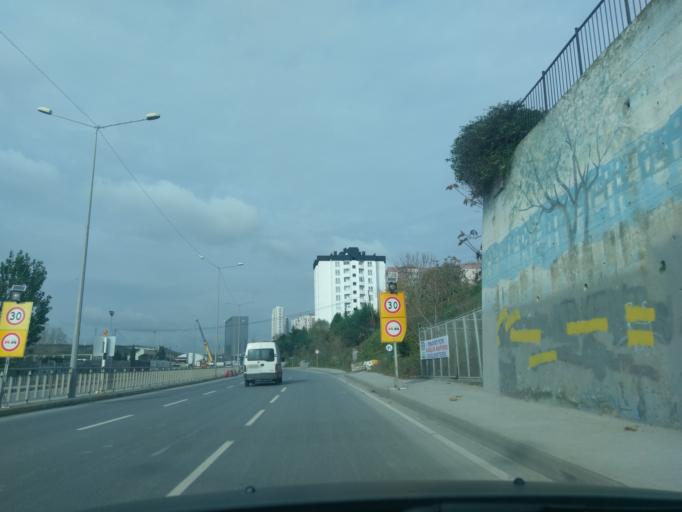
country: TR
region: Istanbul
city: Basaksehir
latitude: 41.0539
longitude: 28.7749
